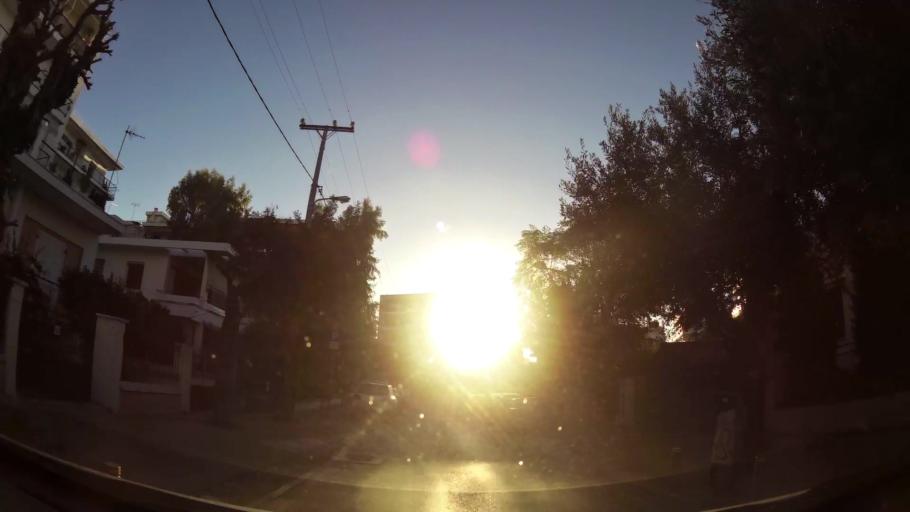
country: GR
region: Attica
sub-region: Nomarchia Athinas
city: Marousi
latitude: 38.0556
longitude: 23.8010
